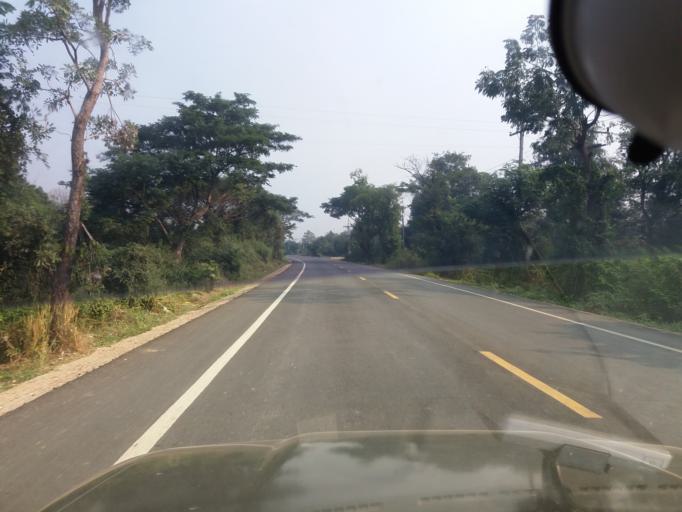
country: TH
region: Sing Buri
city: Bang Racham
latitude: 14.9219
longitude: 100.2651
